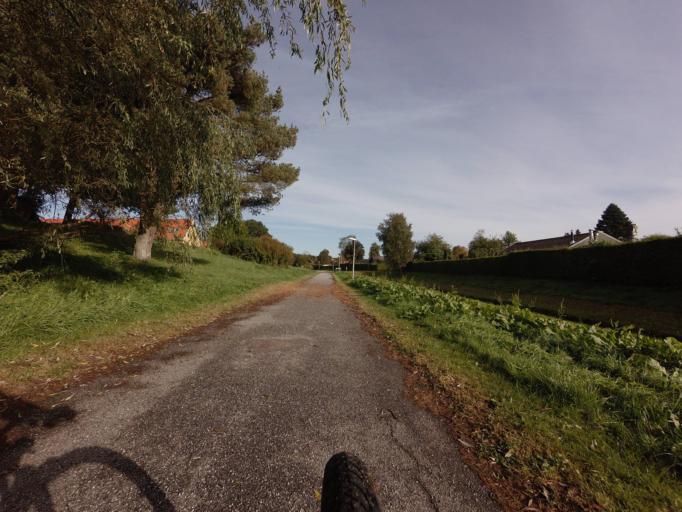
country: DK
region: Central Jutland
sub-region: Viborg Kommune
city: Viborg
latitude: 56.4283
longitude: 9.3959
